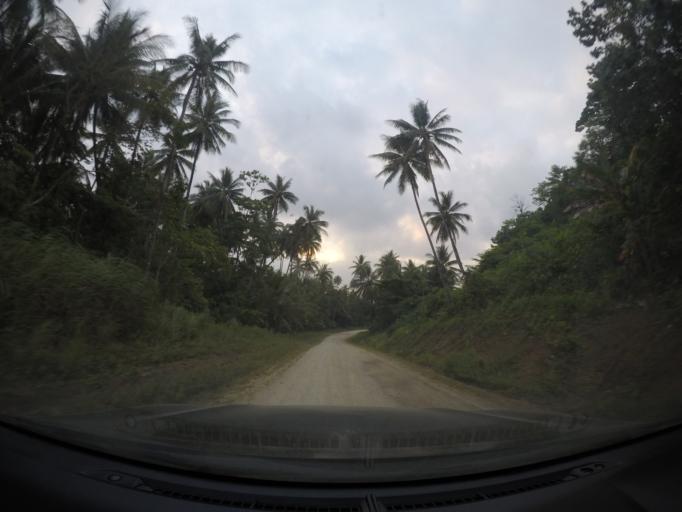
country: PG
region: Milne Bay
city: Alotau
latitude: -10.2986
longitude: 150.7612
